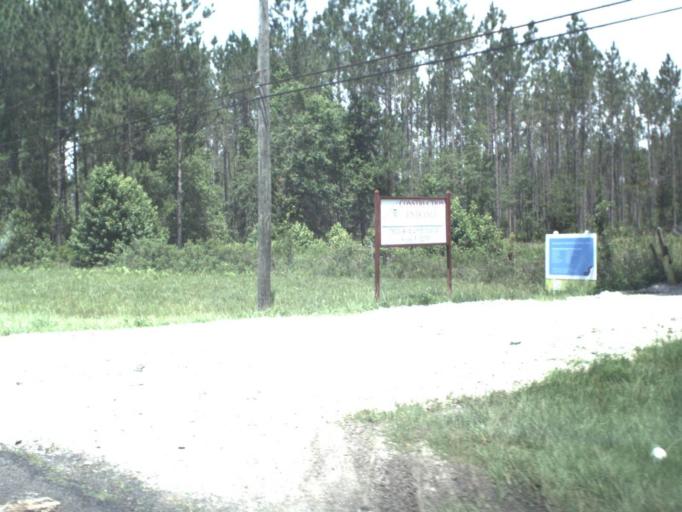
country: US
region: Florida
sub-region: Nassau County
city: Yulee
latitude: 30.6261
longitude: -81.6266
